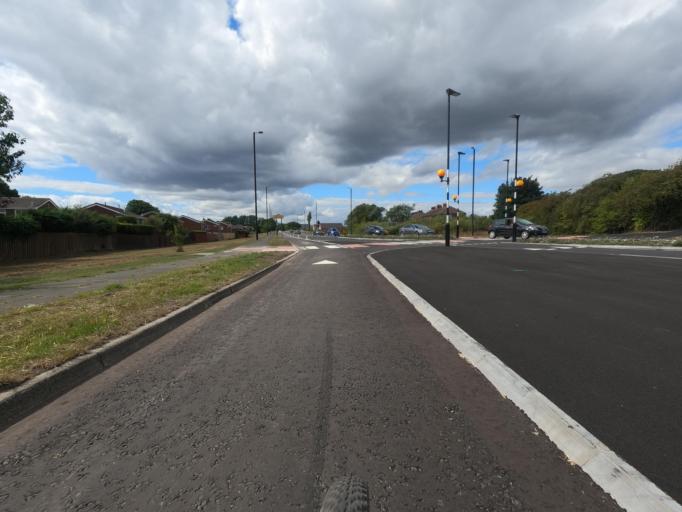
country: GB
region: England
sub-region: Borough of North Tyneside
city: Shiremoor
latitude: 55.0237
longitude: -1.4814
